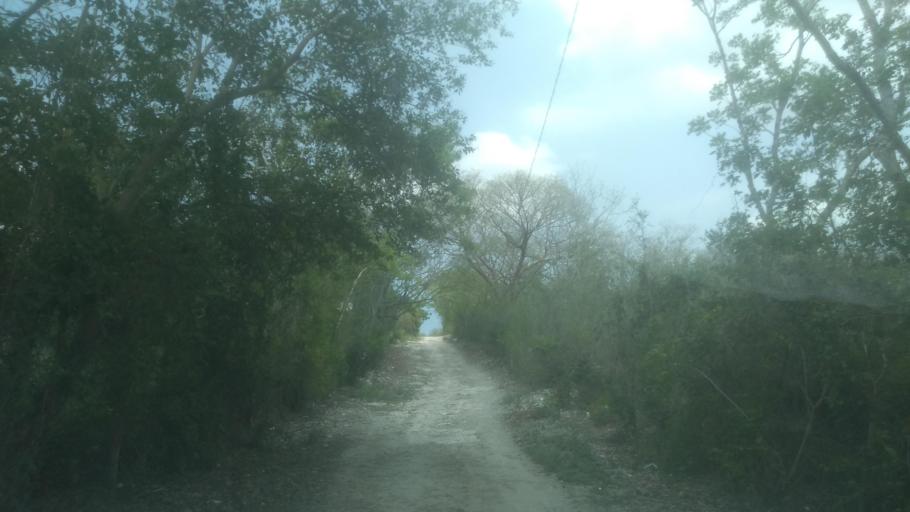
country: MX
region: Veracruz
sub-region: Emiliano Zapata
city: Plan del Rio
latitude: 19.3903
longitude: -96.6333
